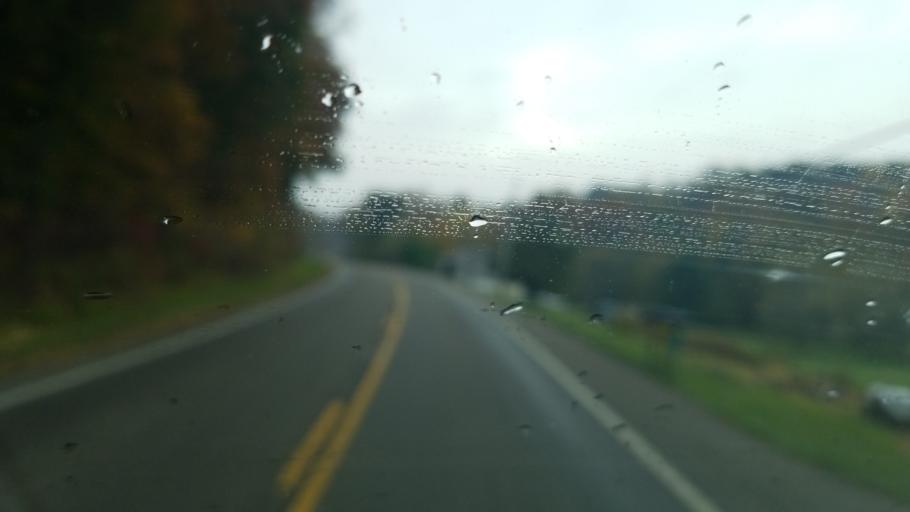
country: US
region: Ohio
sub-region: Holmes County
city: Millersburg
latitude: 40.5100
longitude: -81.9155
